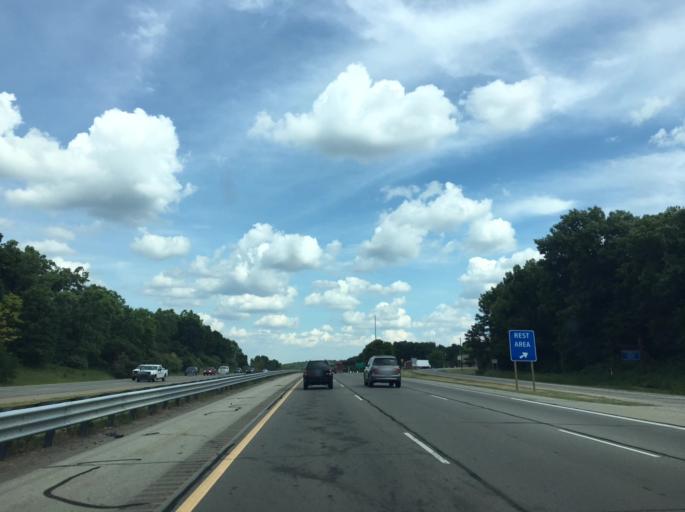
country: US
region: Michigan
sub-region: Oakland County
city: Clarkston
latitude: 42.7450
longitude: -83.4890
